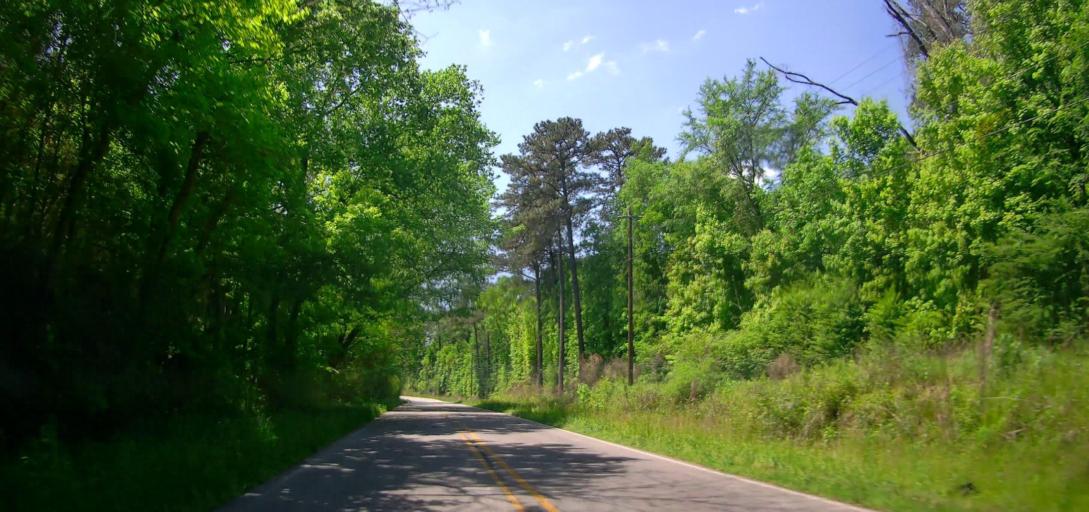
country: US
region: Georgia
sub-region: Bibb County
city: Macon
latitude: 32.8871
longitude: -83.6105
